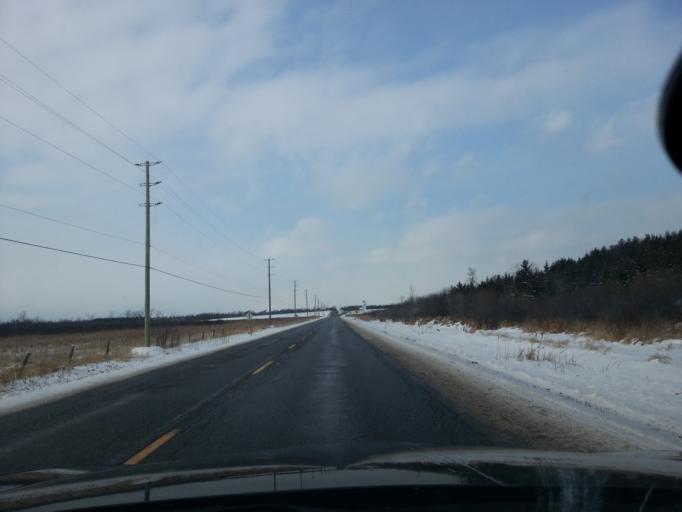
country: CA
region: Ontario
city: Carleton Place
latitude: 45.1647
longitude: -76.0423
